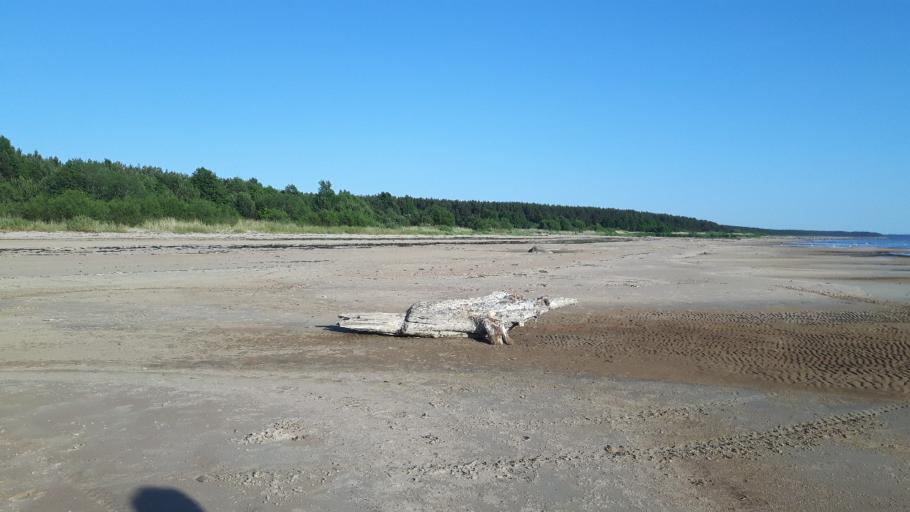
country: LV
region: Salacgrivas
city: Salacgriva
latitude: 57.6885
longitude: 24.3556
